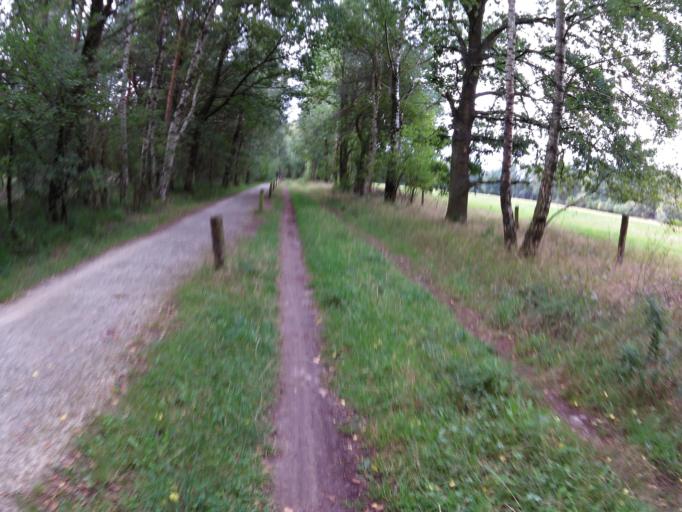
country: DE
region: North Rhine-Westphalia
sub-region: Regierungsbezirk Munster
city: Gronau
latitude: 52.2497
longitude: 7.1028
